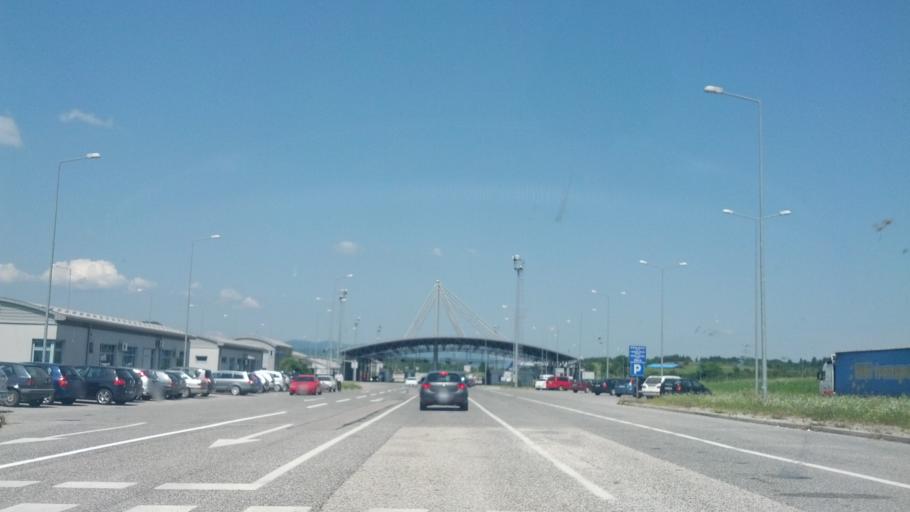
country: BA
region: Federation of Bosnia and Herzegovina
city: Izacic
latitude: 44.8737
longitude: 15.7663
